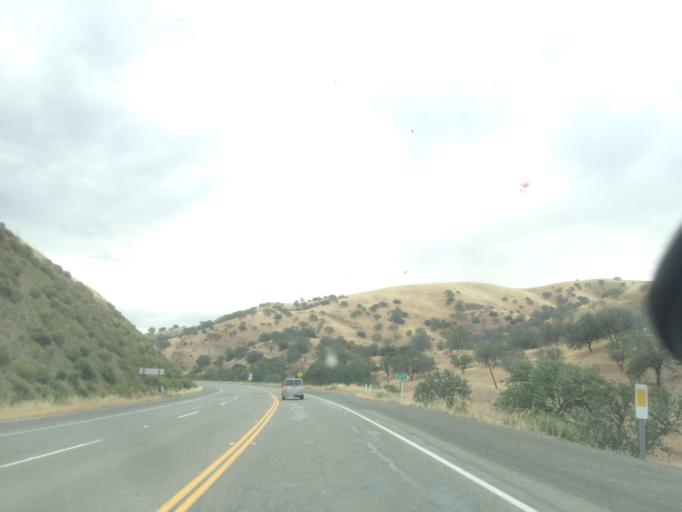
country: US
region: California
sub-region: San Luis Obispo County
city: Shandon
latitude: 35.7792
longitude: -120.1949
